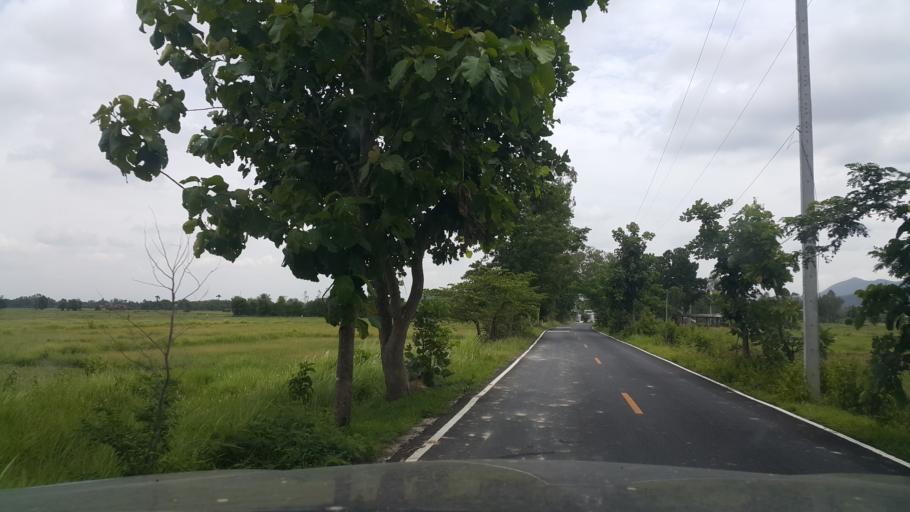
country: TH
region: Lamphun
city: Ban Thi
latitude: 18.6497
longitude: 99.1474
